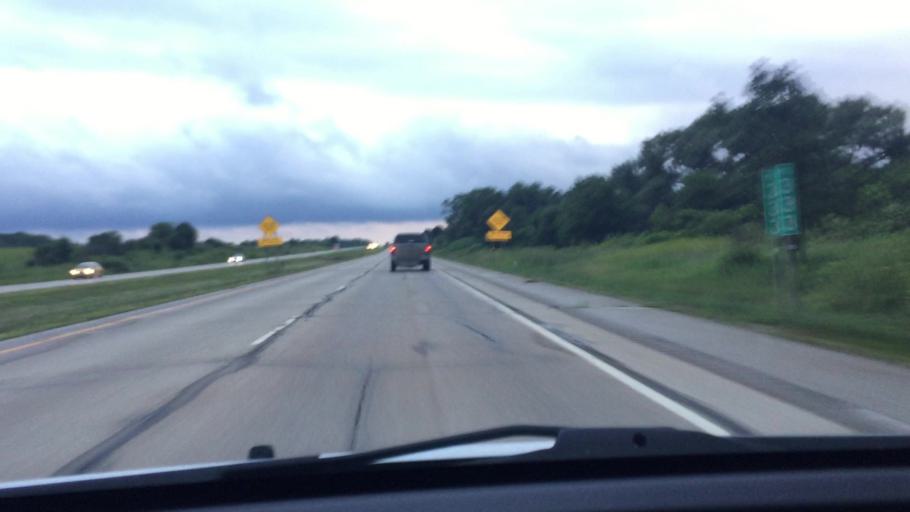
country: US
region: Wisconsin
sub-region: Walworth County
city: Pell Lake
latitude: 42.5674
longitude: -88.3664
